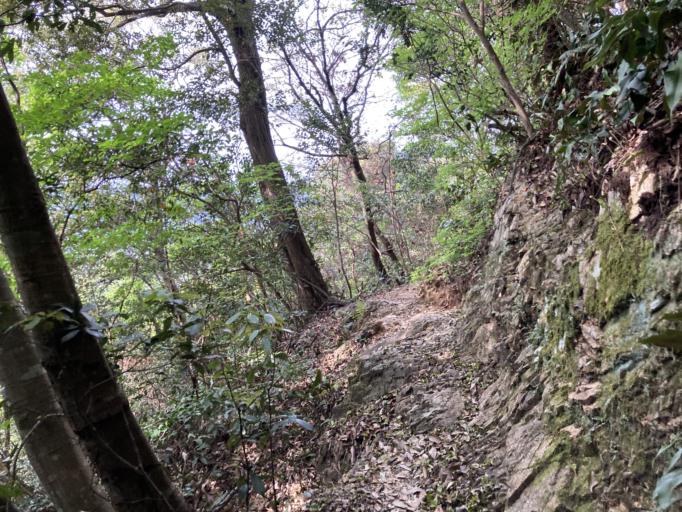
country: JP
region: Shizuoka
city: Kosai-shi
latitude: 34.7436
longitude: 137.4610
